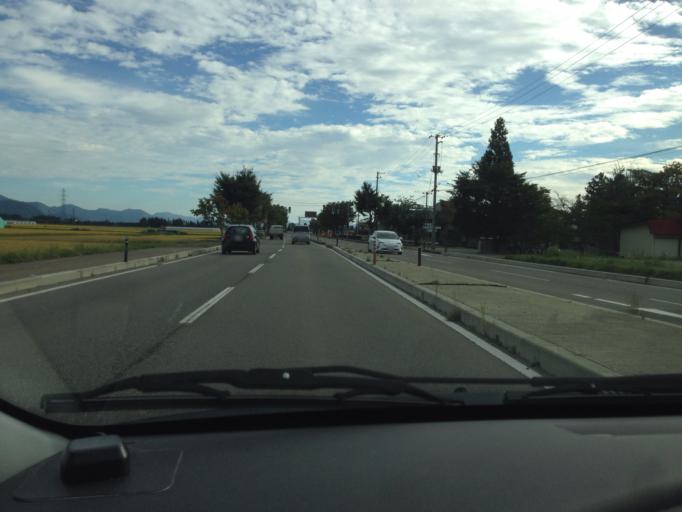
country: JP
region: Fukushima
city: Inawashiro
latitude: 37.5542
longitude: 140.1132
